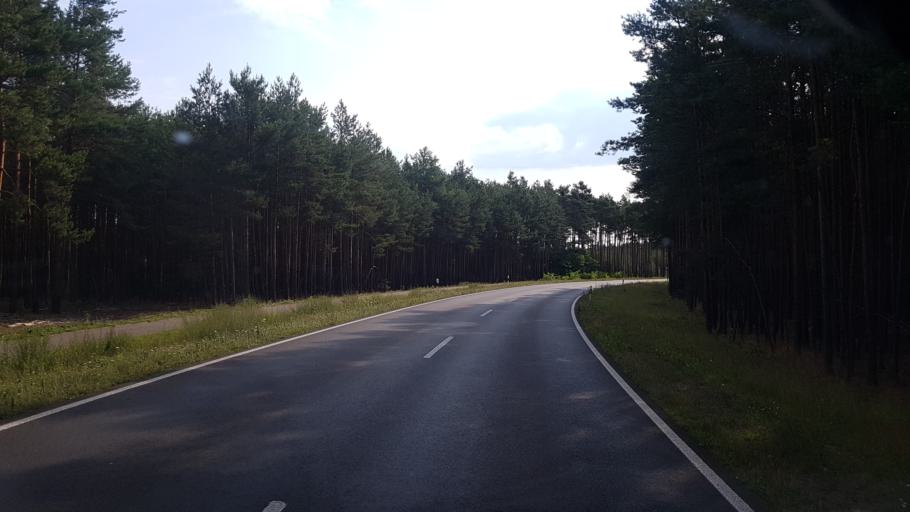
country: DE
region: Brandenburg
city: Golssen
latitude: 52.0513
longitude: 13.5958
